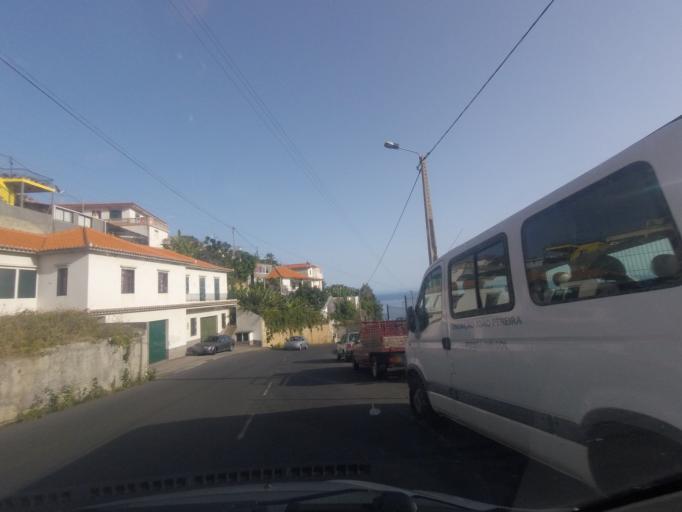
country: PT
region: Madeira
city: Ponta do Sol
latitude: 32.6878
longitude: -17.1074
